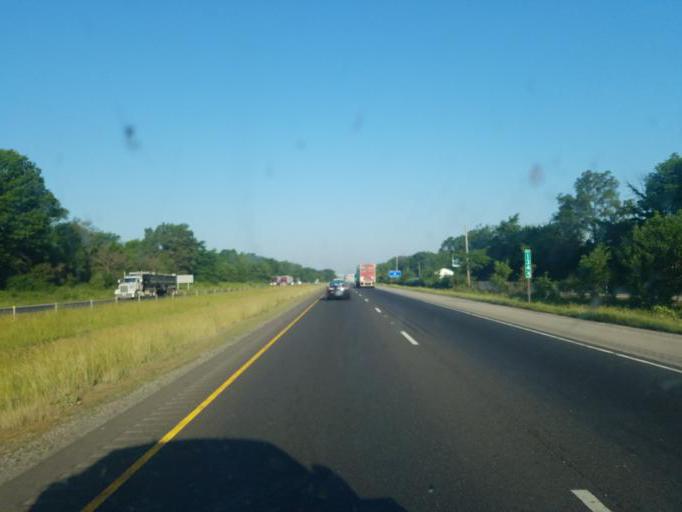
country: US
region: Illinois
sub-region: Will County
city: Ingalls Park
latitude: 41.5131
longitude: -88.0502
